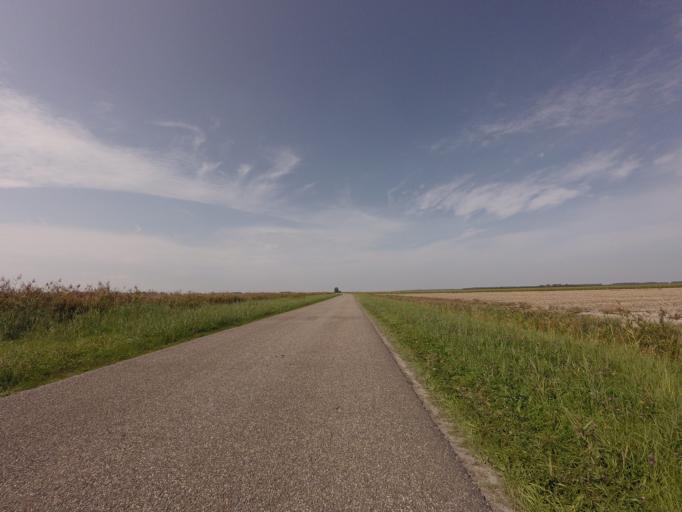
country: NL
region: Groningen
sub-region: Gemeente De Marne
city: Ulrum
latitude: 53.3442
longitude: 6.2791
